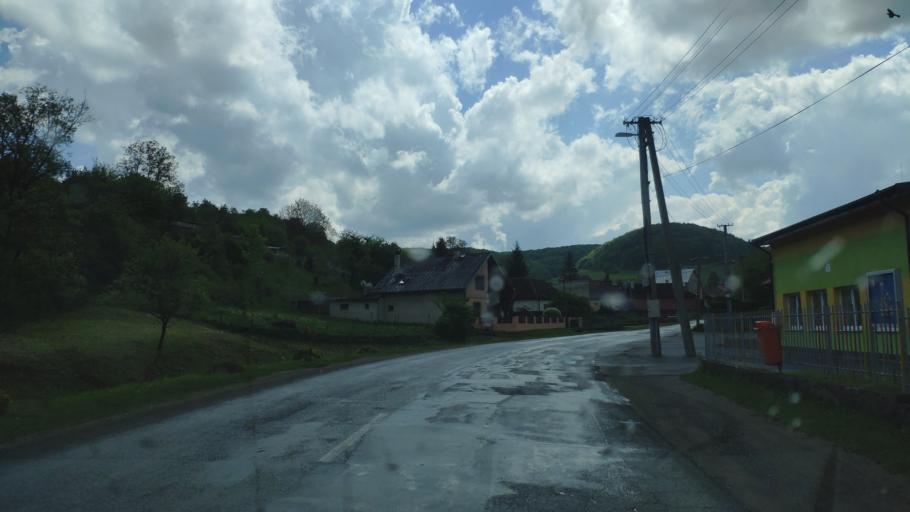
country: SK
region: Presovsky
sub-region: Okres Presov
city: Presov
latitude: 48.9560
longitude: 21.1181
